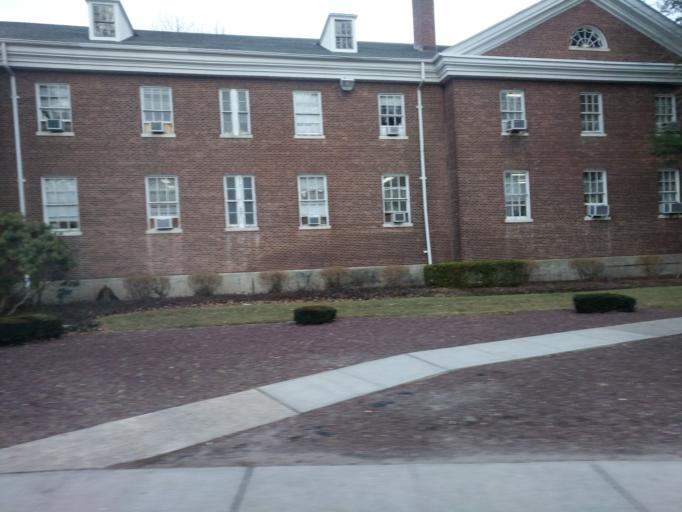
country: US
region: New York
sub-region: Nassau County
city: East Garden City
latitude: 40.7322
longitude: -73.5958
